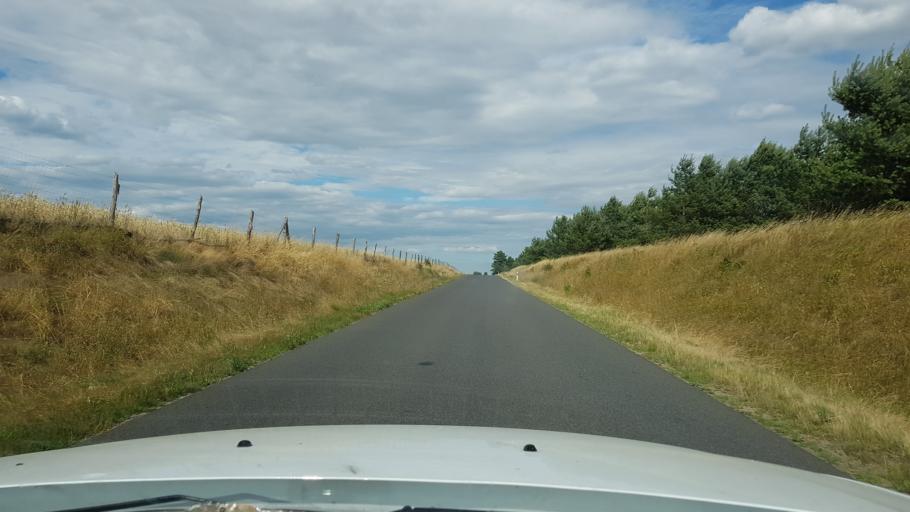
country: PL
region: West Pomeranian Voivodeship
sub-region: Powiat drawski
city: Wierzchowo
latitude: 53.4257
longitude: 16.0511
